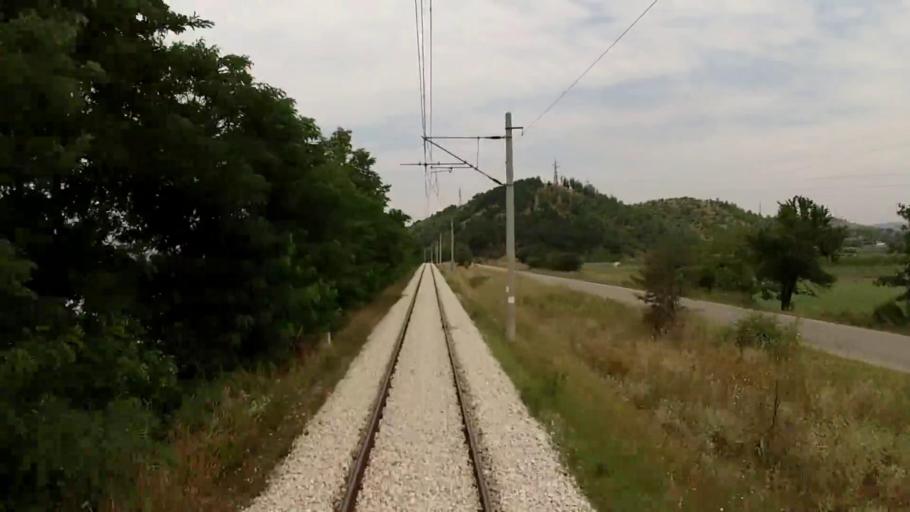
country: BG
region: Blagoevgrad
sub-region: Obshtina Blagoevgrad
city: Blagoevgrad
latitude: 41.9655
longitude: 23.0996
